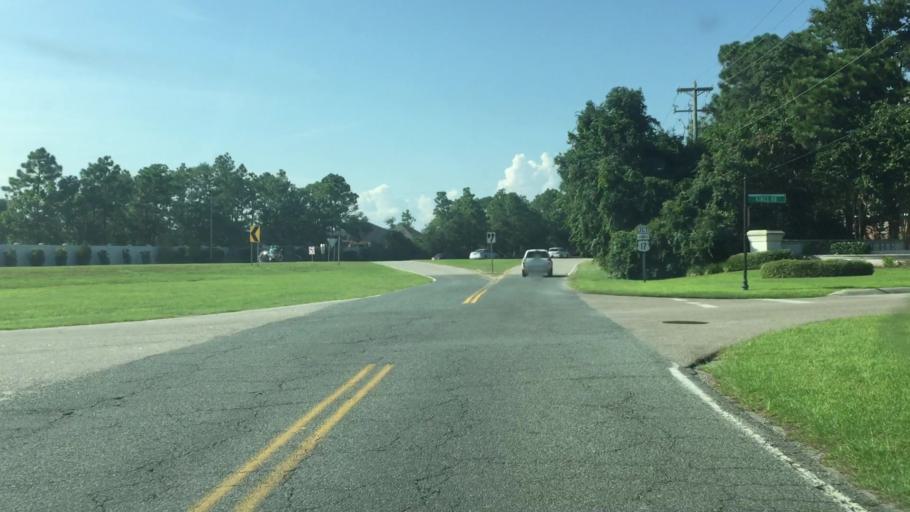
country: US
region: South Carolina
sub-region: Horry County
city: Myrtle Beach
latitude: 33.7569
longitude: -78.8067
